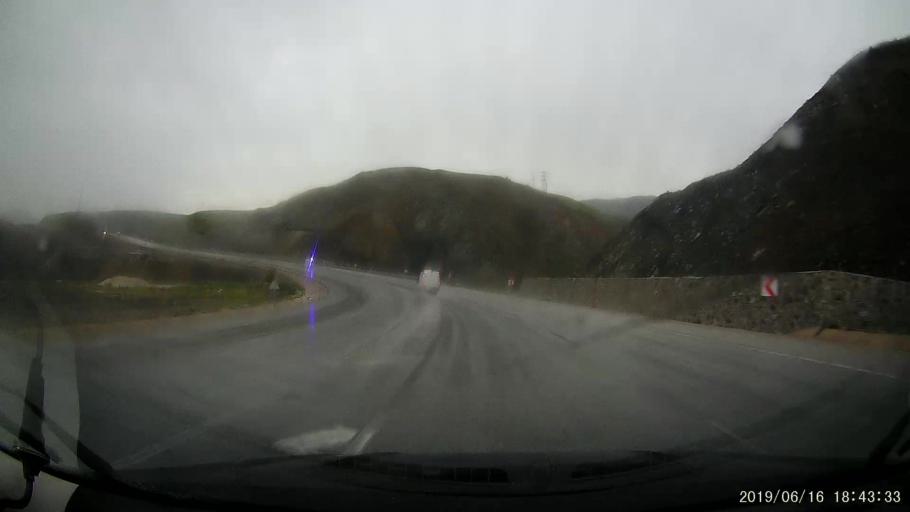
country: TR
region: Erzincan
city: Doganbeyli
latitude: 39.8711
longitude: 39.0909
